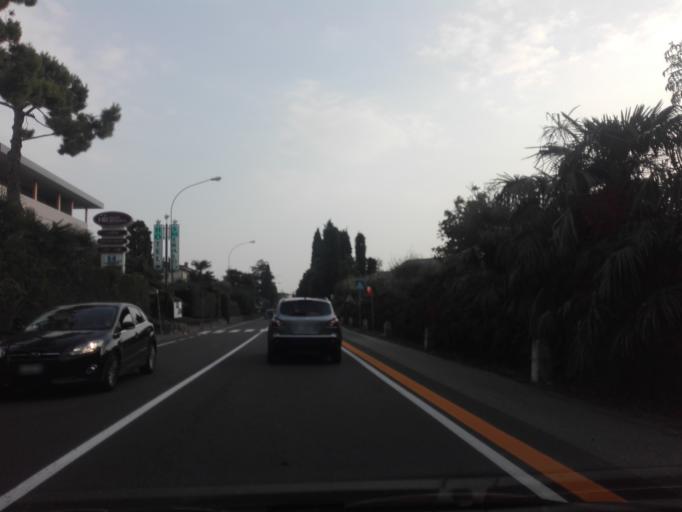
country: IT
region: Veneto
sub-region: Provincia di Verona
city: Lazise
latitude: 45.5104
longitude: 10.7333
